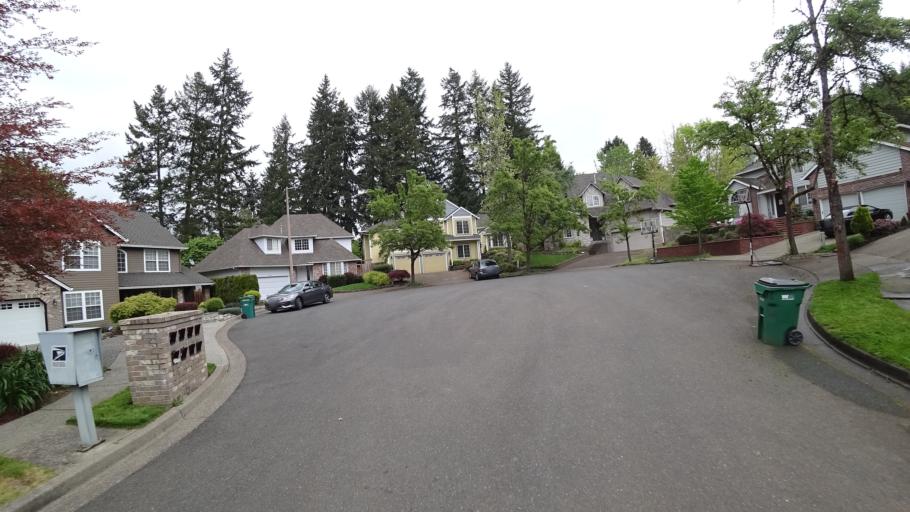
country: US
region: Oregon
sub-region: Washington County
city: Beaverton
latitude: 45.4606
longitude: -122.8320
